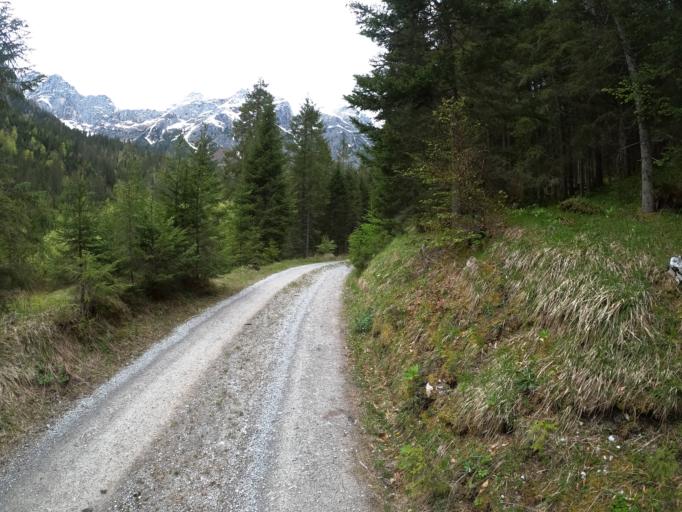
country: AT
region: Salzburg
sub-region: Politischer Bezirk Zell am See
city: Dienten am Hochkonig
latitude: 47.4666
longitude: 13.0536
